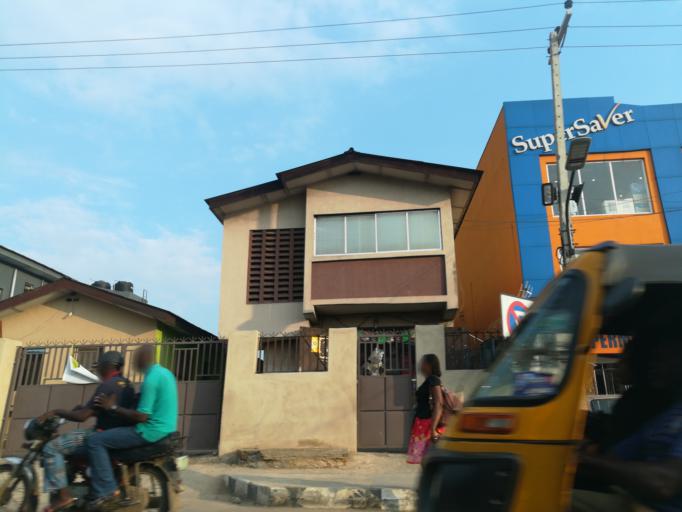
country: NG
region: Lagos
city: Ojota
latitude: 6.5863
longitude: 3.3937
